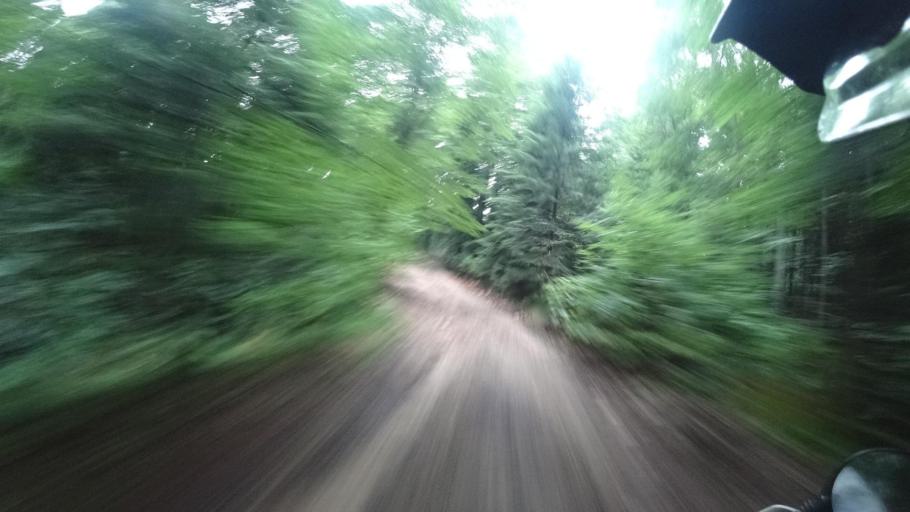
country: HR
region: Licko-Senjska
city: Jezerce
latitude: 44.8044
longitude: 15.6435
